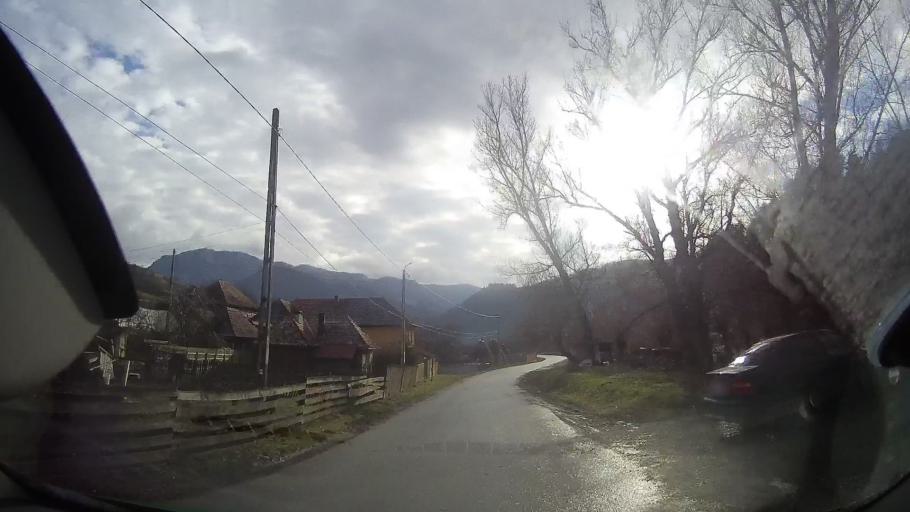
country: RO
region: Alba
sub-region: Comuna Ocolis
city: Ocolis
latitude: 46.4822
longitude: 23.4635
